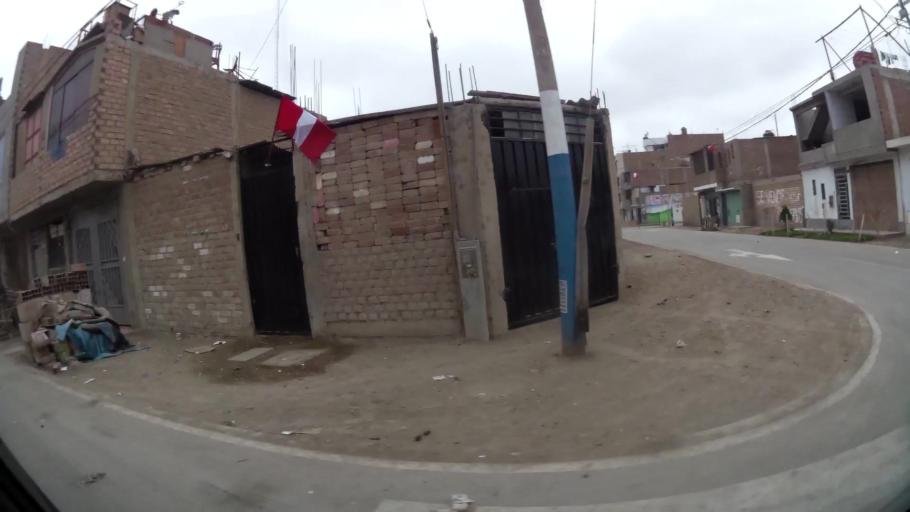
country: PE
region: Lima
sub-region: Lima
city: Independencia
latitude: -11.9771
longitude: -77.0987
